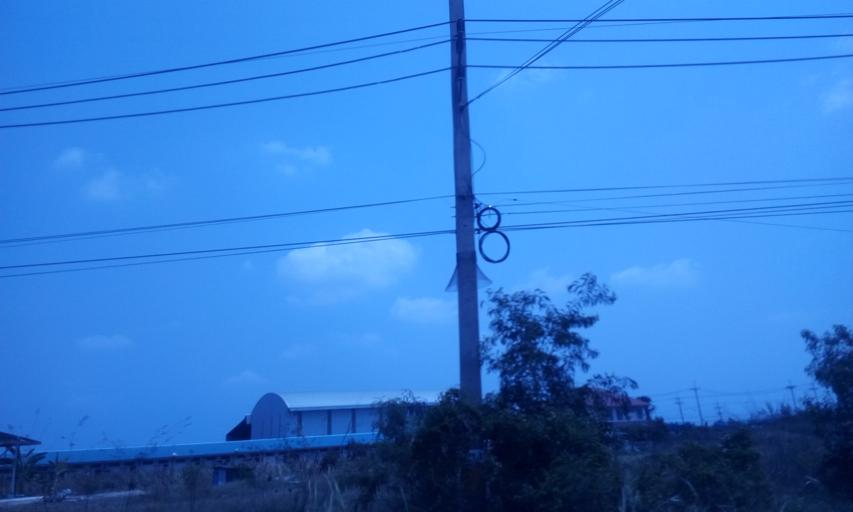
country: TH
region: Chachoengsao
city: Bang Nam Priao
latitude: 13.8333
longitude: 101.0555
